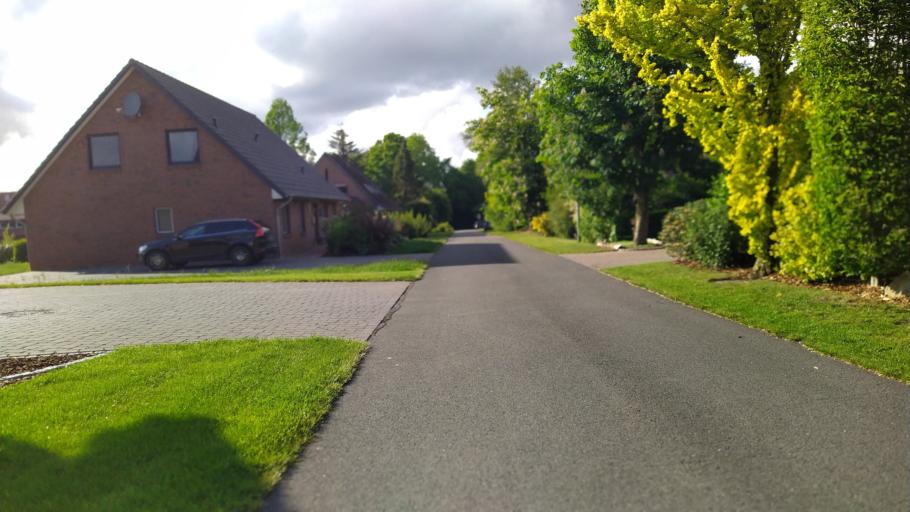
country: DE
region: Lower Saxony
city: Farven
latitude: 53.4349
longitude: 9.3267
